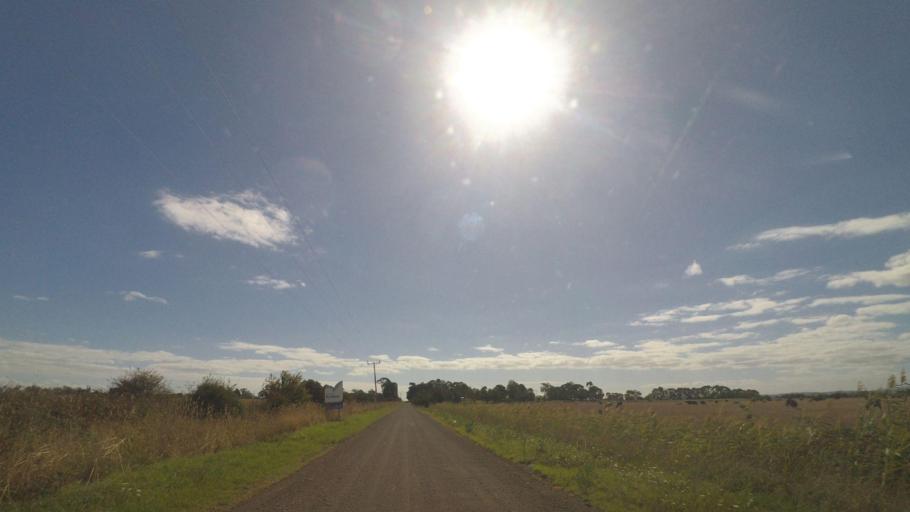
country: AU
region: Victoria
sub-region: Cardinia
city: Pakenham South
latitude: -38.1375
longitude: 145.4726
